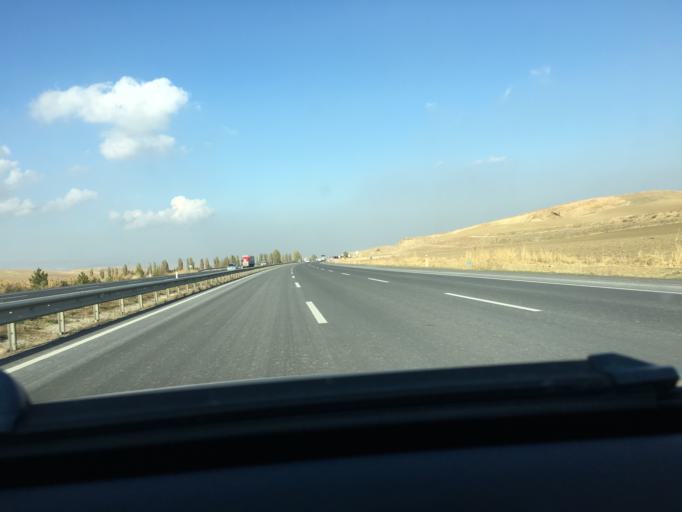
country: TR
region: Ankara
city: Polatli
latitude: 39.6278
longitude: 32.1943
